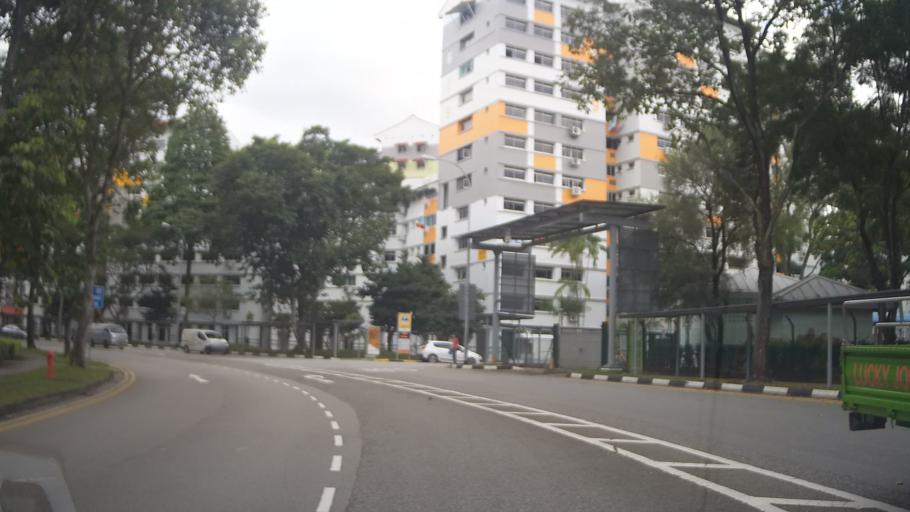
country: MY
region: Johor
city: Johor Bahru
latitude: 1.3990
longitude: 103.7458
